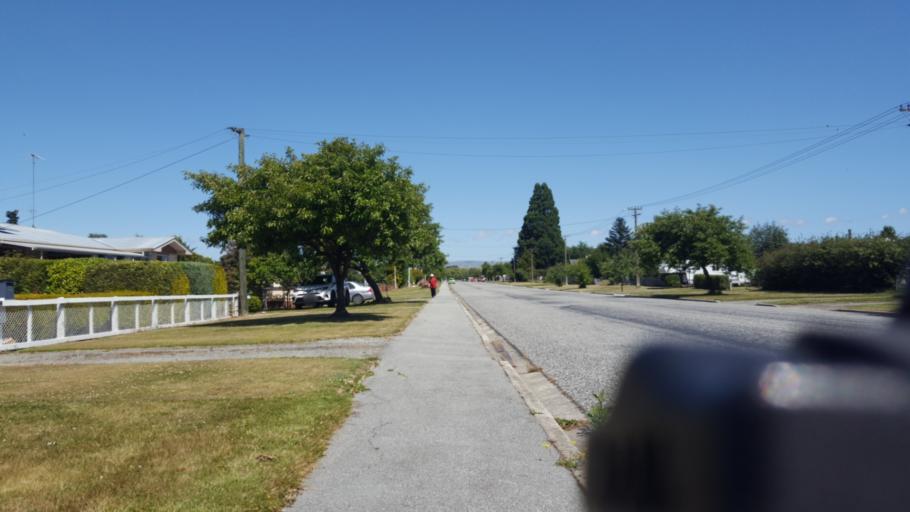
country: NZ
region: Otago
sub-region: Dunedin City
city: Dunedin
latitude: -45.1269
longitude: 170.1054
